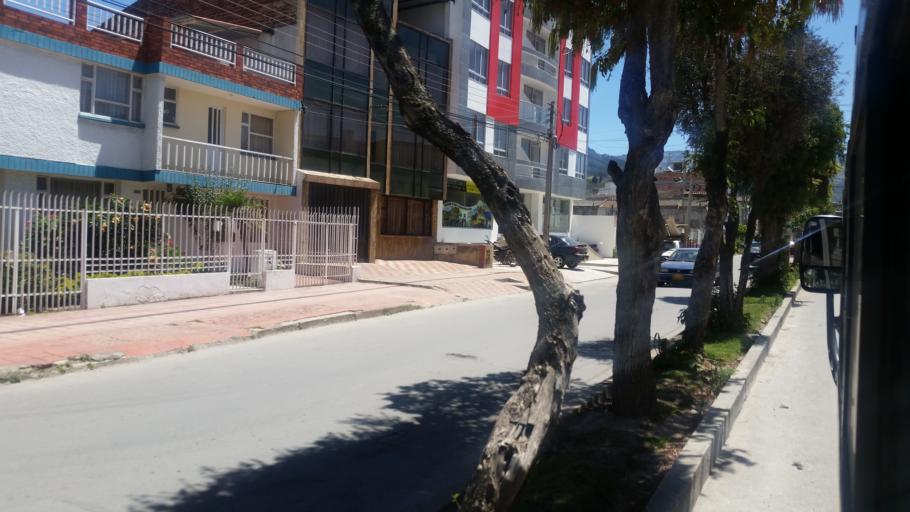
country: CO
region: Boyaca
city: Sogamoso
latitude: 5.7217
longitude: -72.9299
